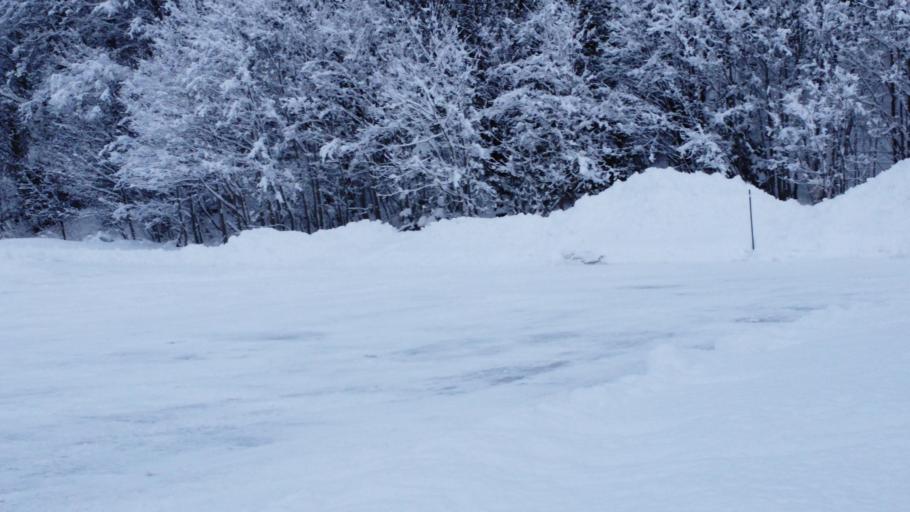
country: NO
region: Nordland
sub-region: Rana
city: Mo i Rana
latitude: 66.3353
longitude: 14.1404
